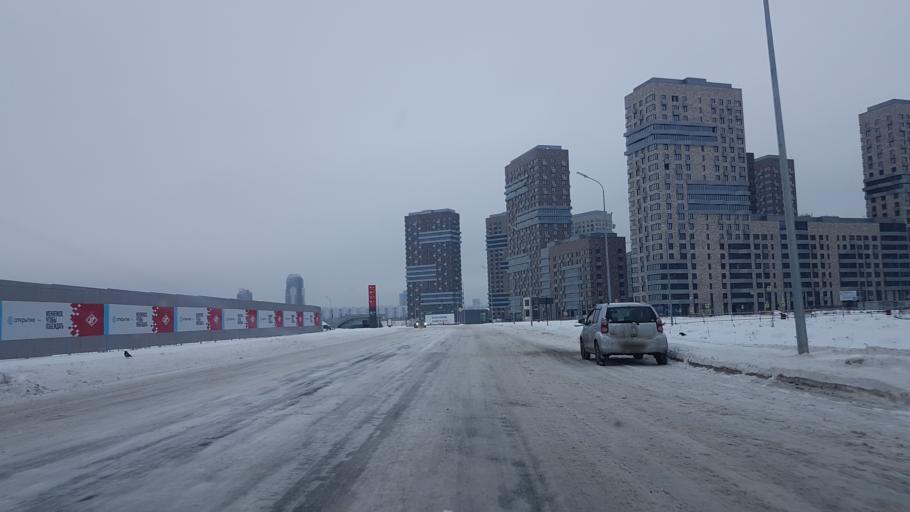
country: RU
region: Moscow
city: Strogino
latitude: 55.8190
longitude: 37.4359
